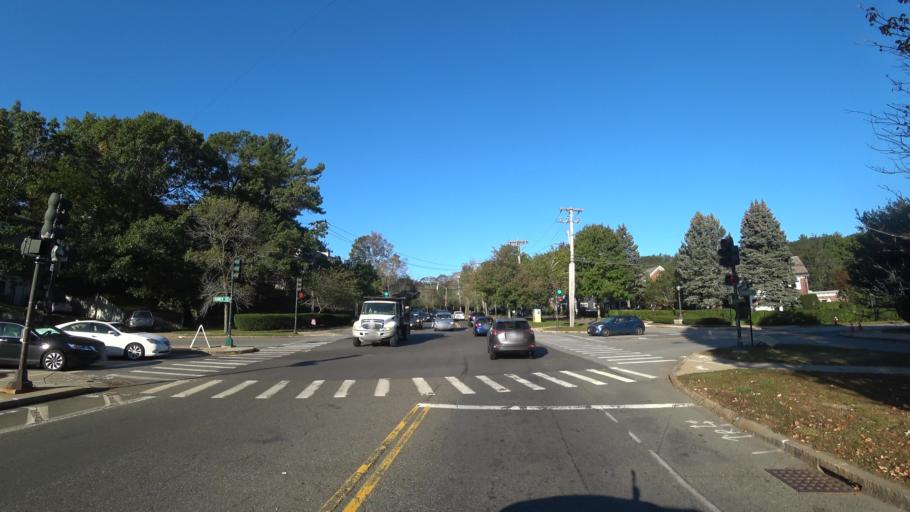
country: US
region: Massachusetts
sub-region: Middlesex County
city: Newton
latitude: 42.3381
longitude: -71.2114
